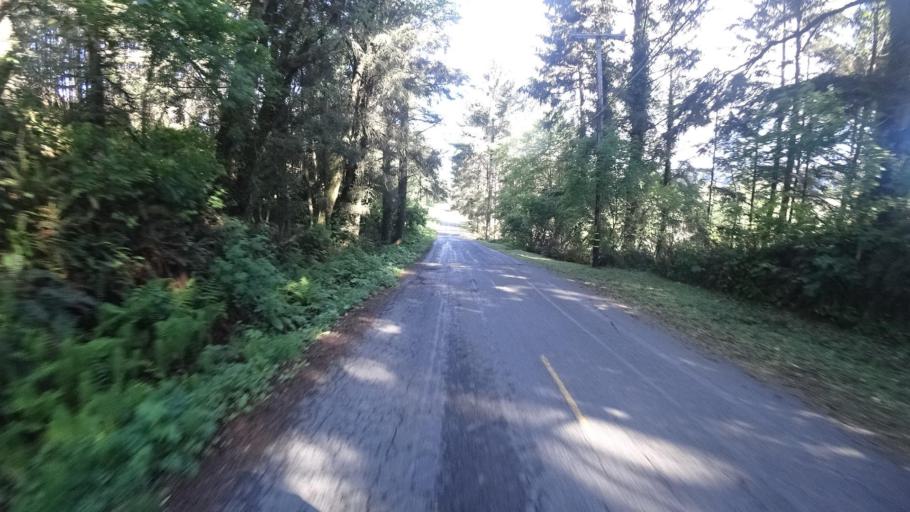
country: US
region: California
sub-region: Humboldt County
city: Westhaven-Moonstone
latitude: 41.0096
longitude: -124.1069
